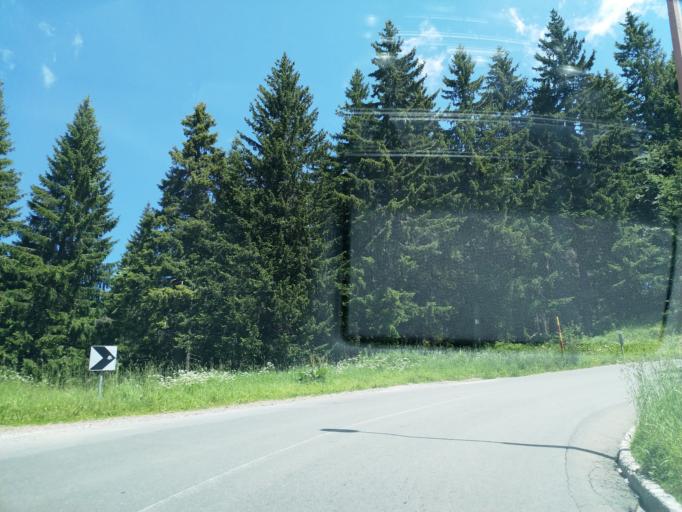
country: RS
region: Central Serbia
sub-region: Raski Okrug
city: Raska
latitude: 43.2877
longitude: 20.7960
